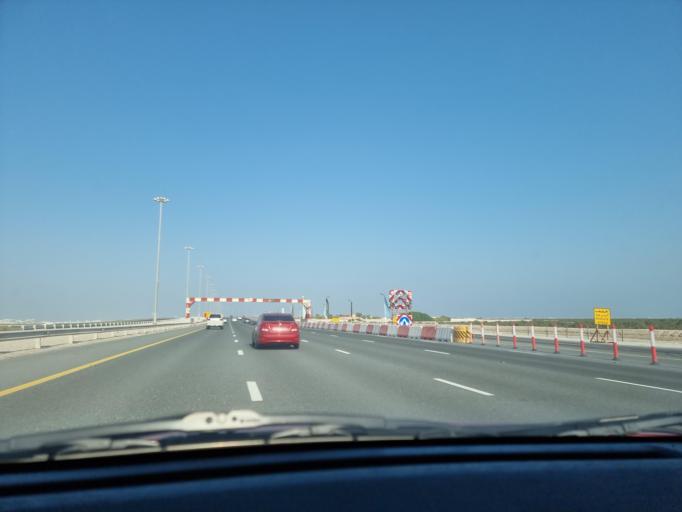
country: AE
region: Abu Dhabi
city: Abu Dhabi
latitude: 24.5259
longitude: 54.5045
